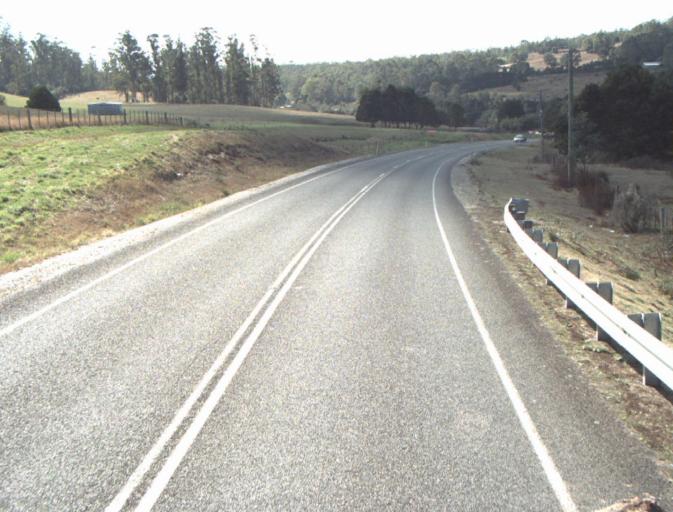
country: AU
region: Tasmania
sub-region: Launceston
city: Mayfield
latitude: -41.2835
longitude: 147.2185
